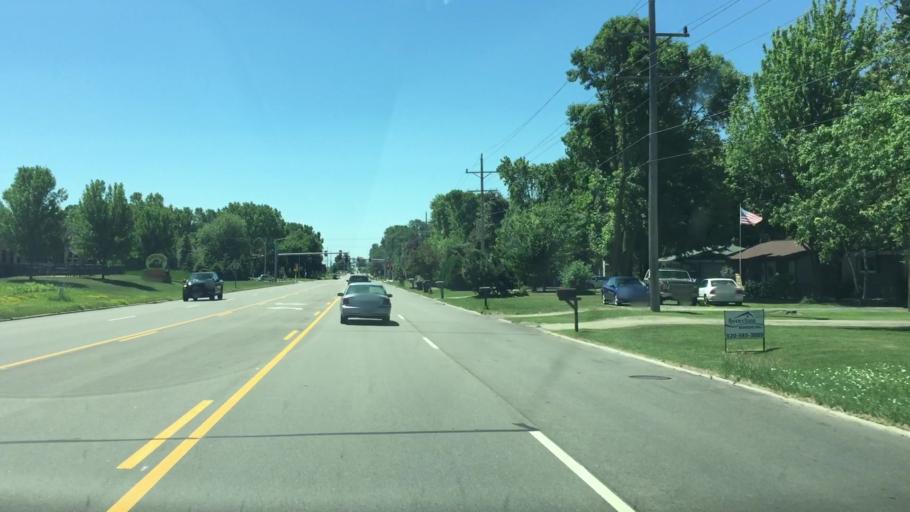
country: US
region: Wisconsin
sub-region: Outagamie County
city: Appleton
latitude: 44.2206
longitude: -88.4042
